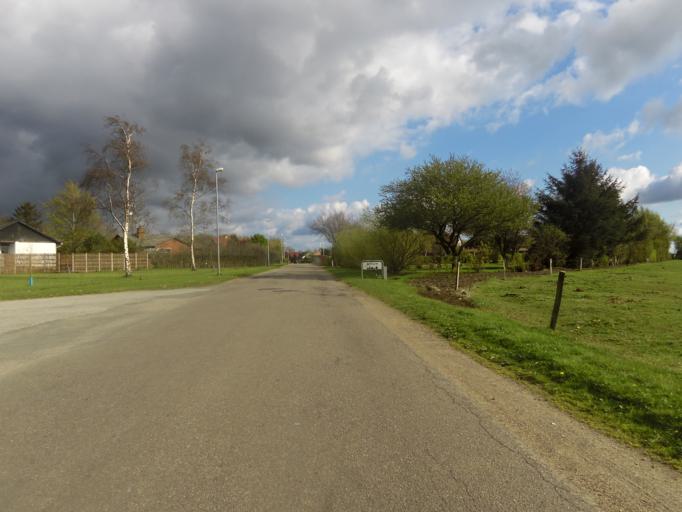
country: DK
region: South Denmark
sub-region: Haderslev Kommune
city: Gram
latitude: 55.2532
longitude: 8.9595
